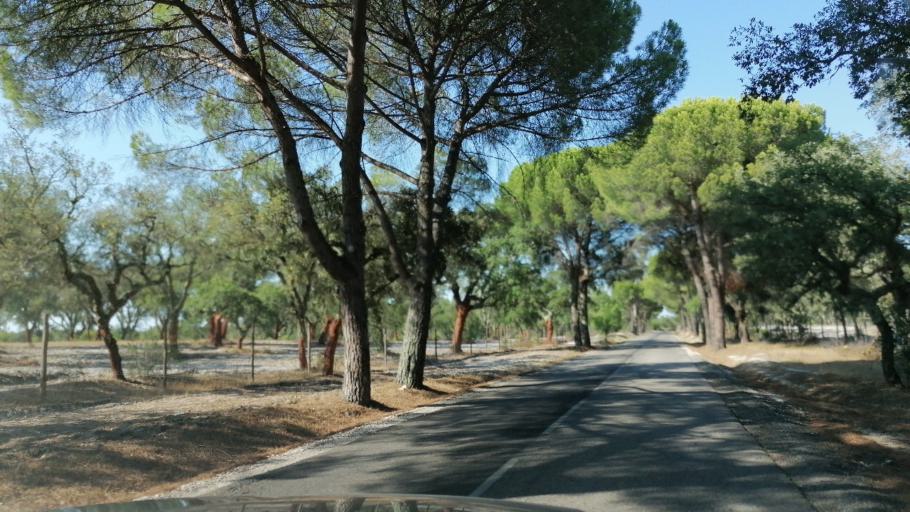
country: PT
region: Santarem
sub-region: Coruche
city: Coruche
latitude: 38.8125
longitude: -8.5756
